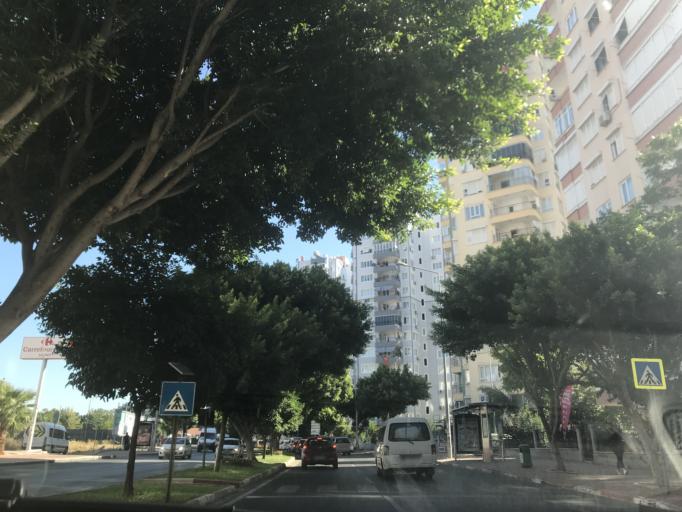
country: TR
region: Antalya
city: Antalya
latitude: 36.8983
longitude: 30.6303
